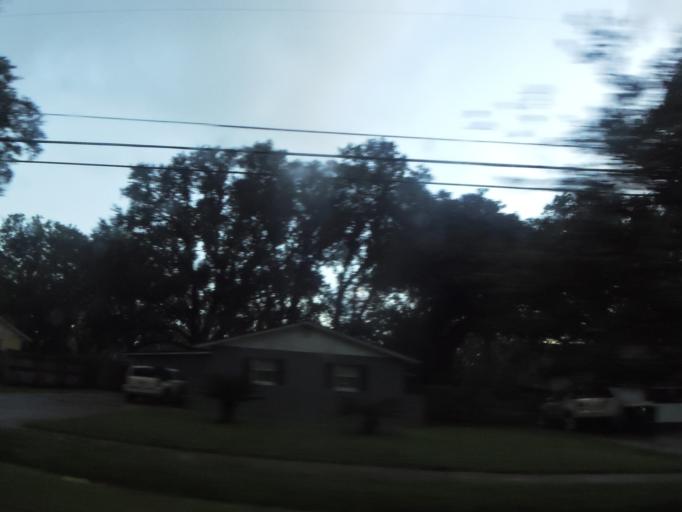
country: US
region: Florida
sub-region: Duval County
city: Jacksonville
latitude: 30.2472
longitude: -81.6190
